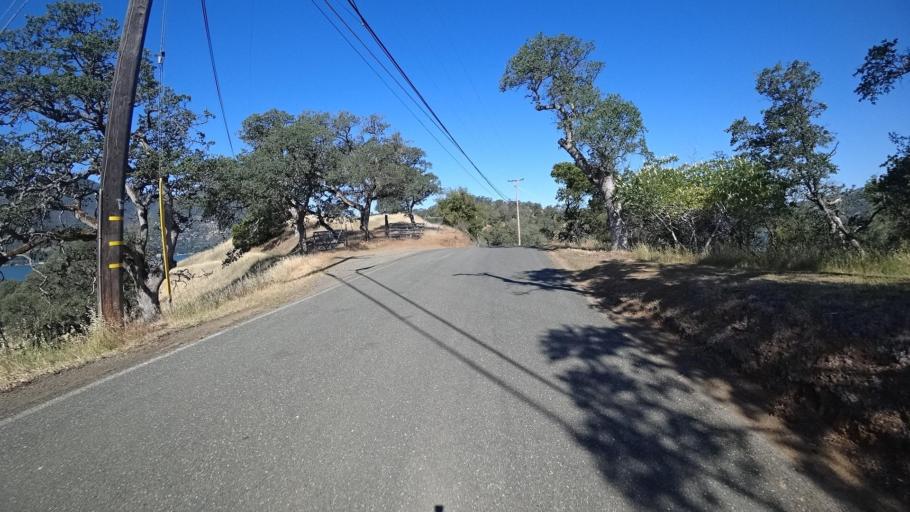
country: US
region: California
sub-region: Lake County
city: Clearlake Oaks
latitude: 39.0050
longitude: -122.7189
